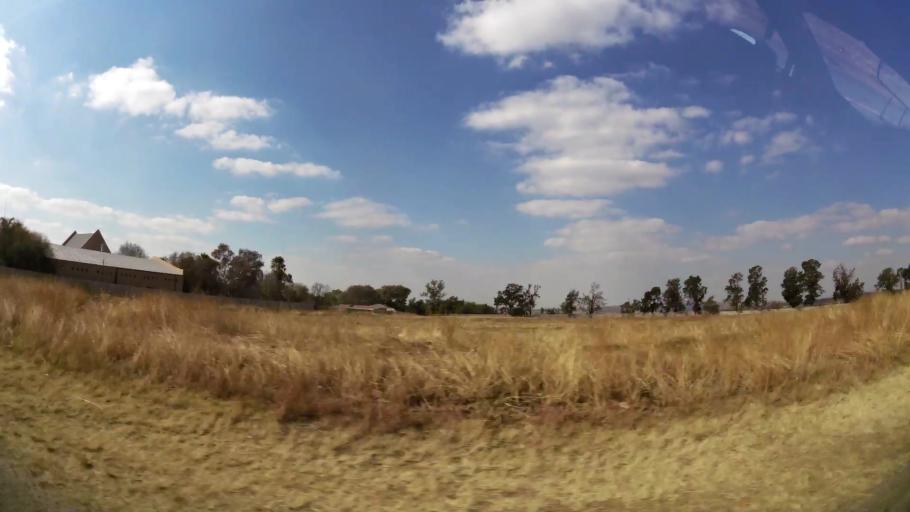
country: ZA
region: Gauteng
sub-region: West Rand District Municipality
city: Krugersdorp
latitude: -26.0646
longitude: 27.7609
